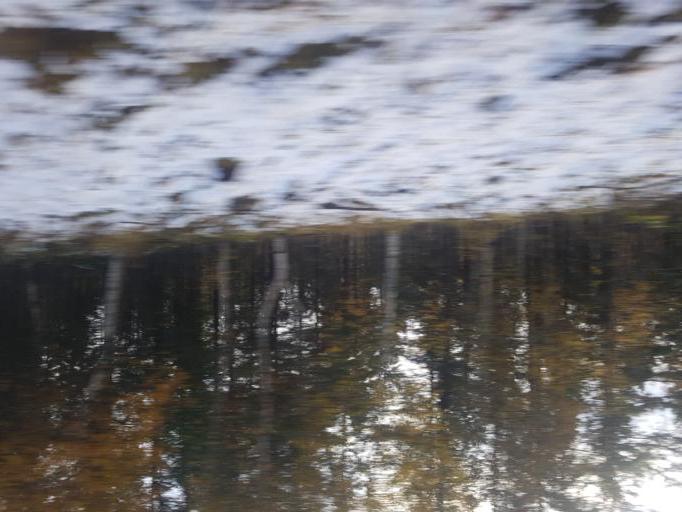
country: NO
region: Sor-Trondelag
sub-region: Oppdal
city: Oppdal
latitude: 62.6308
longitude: 9.7882
